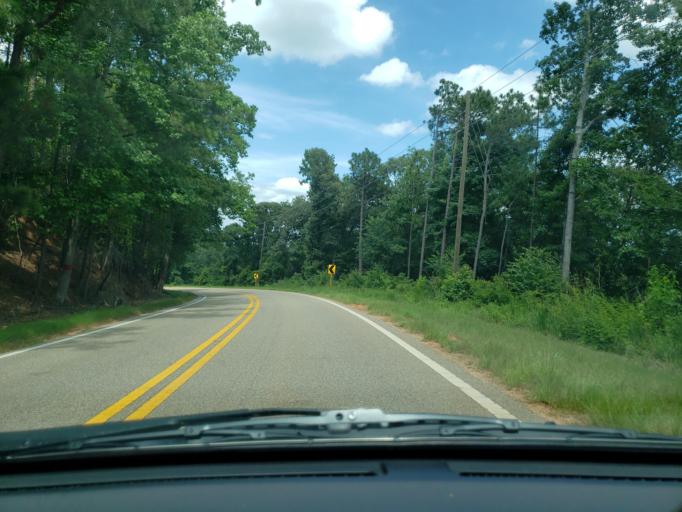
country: US
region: Alabama
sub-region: Elmore County
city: Eclectic
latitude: 32.6722
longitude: -85.9149
